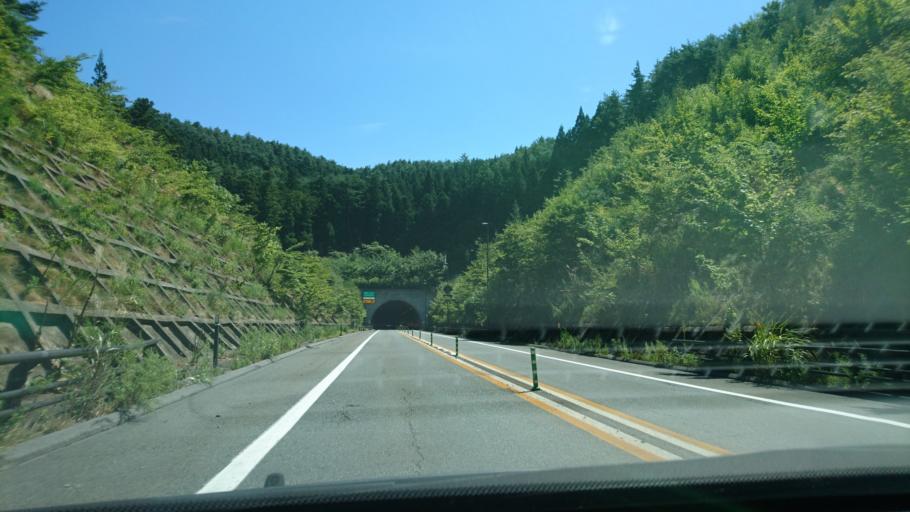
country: JP
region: Iwate
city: Kamaishi
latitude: 39.2439
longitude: 141.7328
